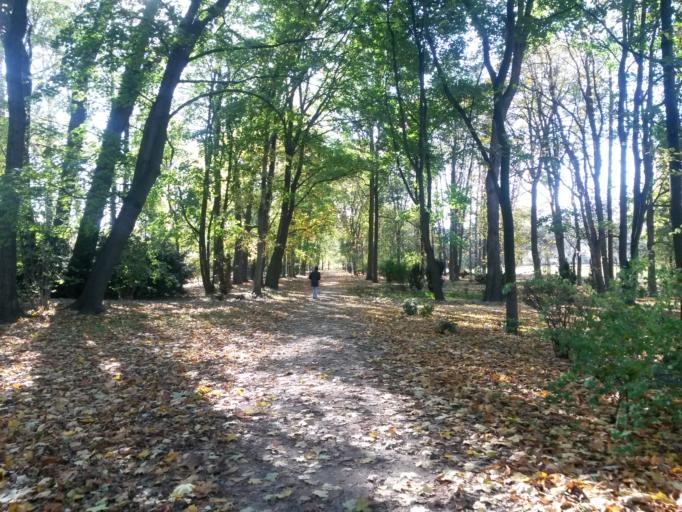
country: PL
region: Masovian Voivodeship
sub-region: Warszawa
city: Mokotow
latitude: 52.2090
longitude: 21.0347
